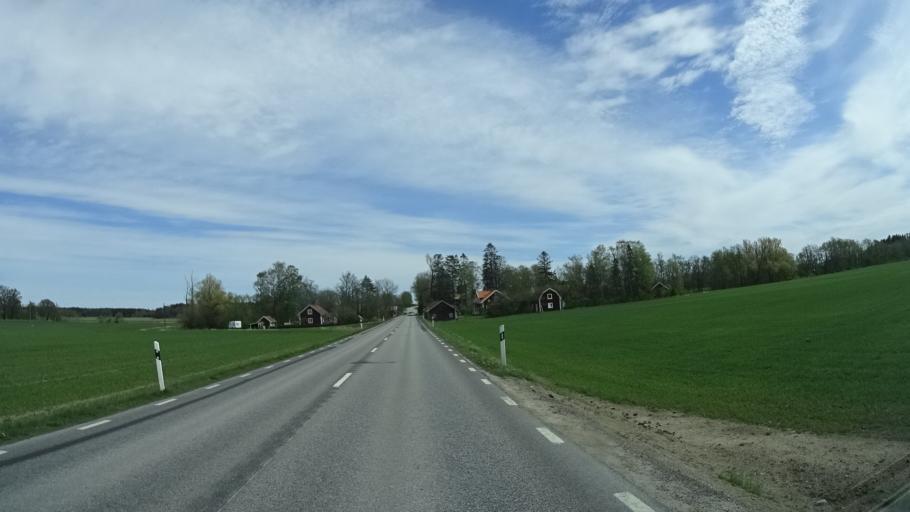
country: SE
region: OEstergoetland
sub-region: Linkopings Kommun
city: Vikingstad
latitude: 58.3706
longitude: 15.3703
